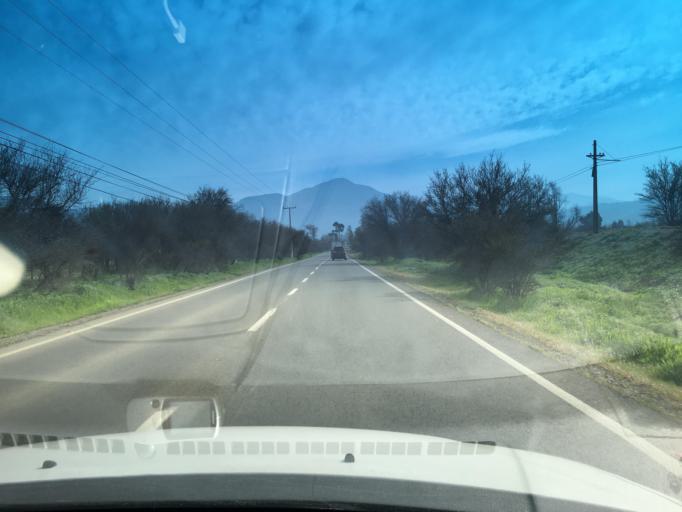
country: CL
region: Santiago Metropolitan
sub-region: Provincia de Chacabuco
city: Lampa
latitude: -33.1260
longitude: -70.9232
